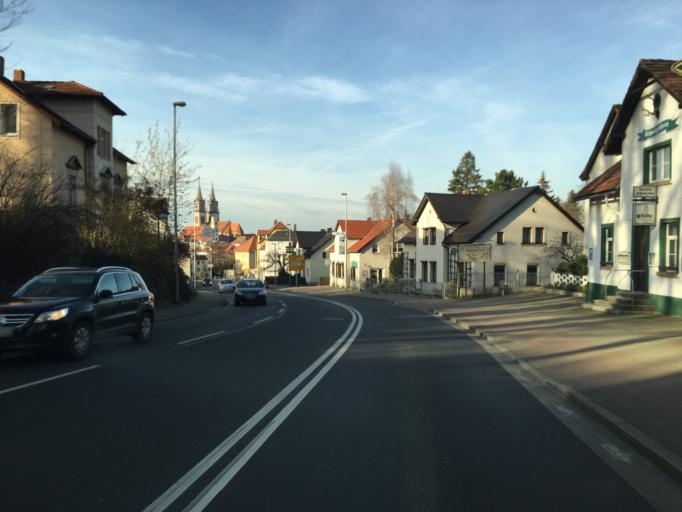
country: DE
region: Saxony
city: Oschatz
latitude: 51.2955
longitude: 13.1167
